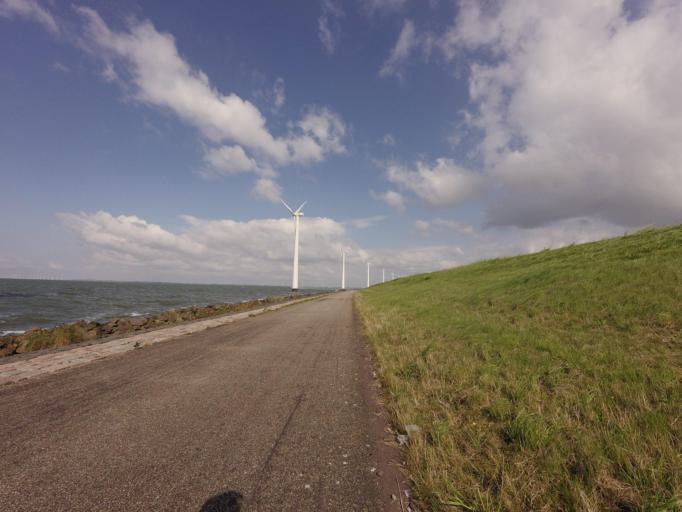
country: NL
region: Flevoland
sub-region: Gemeente Urk
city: Urk
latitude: 52.5938
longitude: 5.5629
